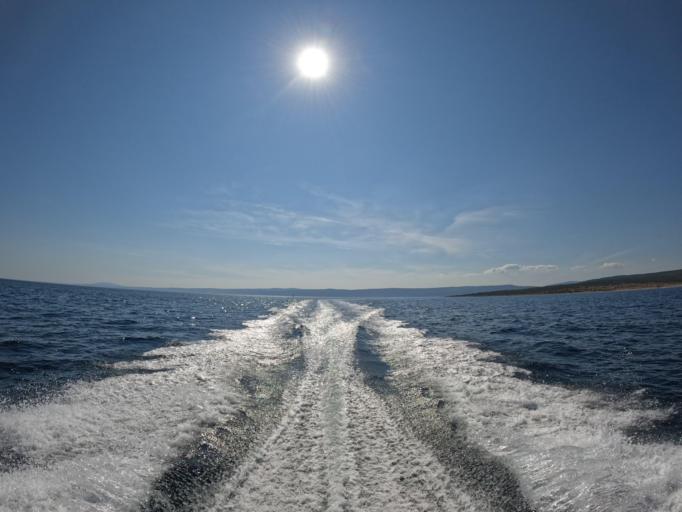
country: HR
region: Primorsko-Goranska
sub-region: Grad Krk
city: Krk
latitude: 44.9535
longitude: 14.5635
